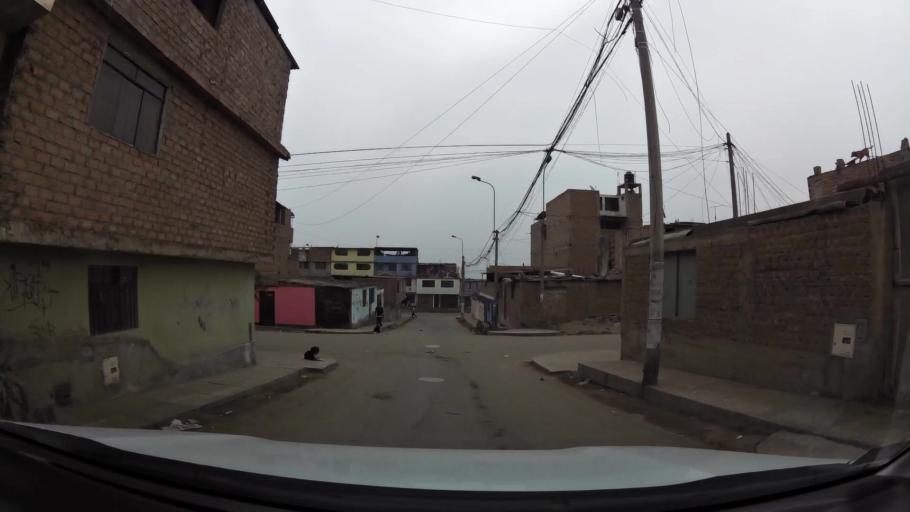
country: PE
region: Lima
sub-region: Lima
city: Surco
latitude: -12.1771
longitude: -76.9619
